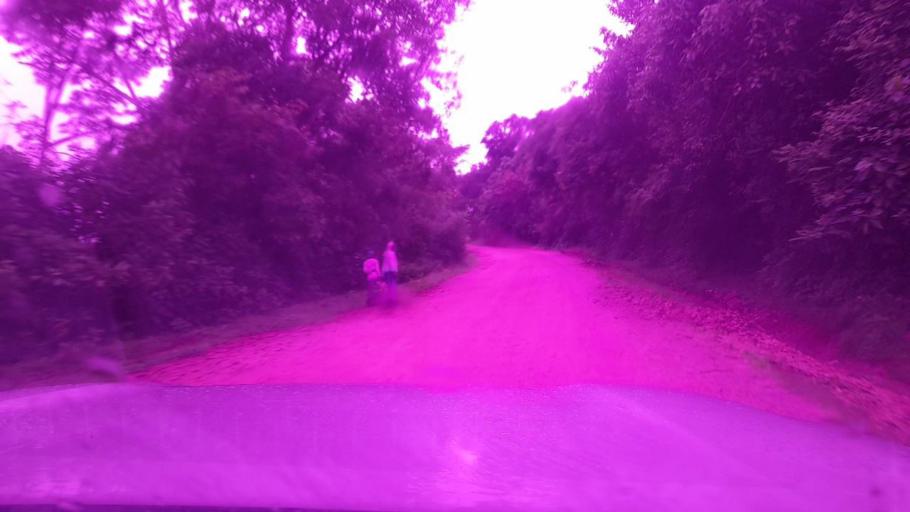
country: ET
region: Southern Nations, Nationalities, and People's Region
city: Bonga
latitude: 7.4489
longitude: 36.1322
